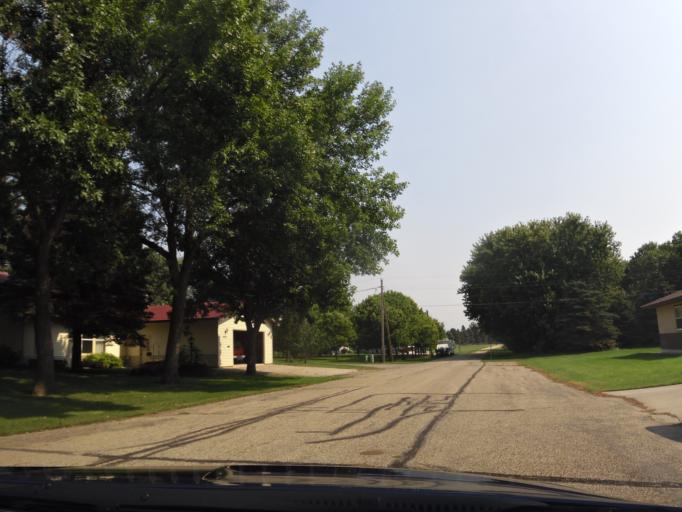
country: US
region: South Dakota
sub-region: Roberts County
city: Sisseton
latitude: 46.0733
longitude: -97.1432
